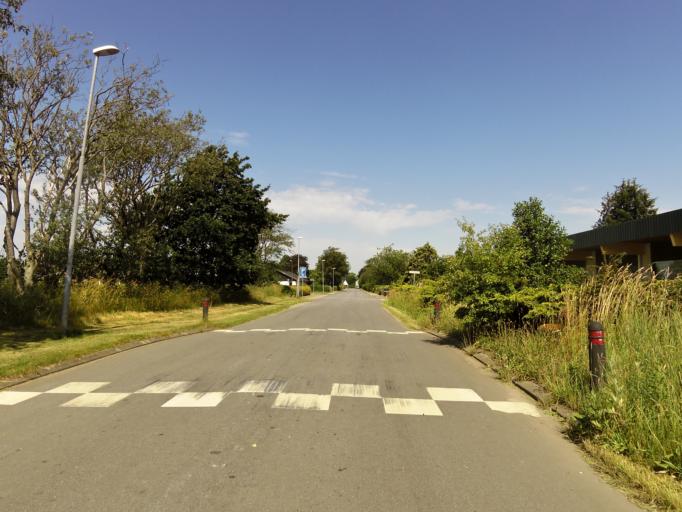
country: DK
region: South Denmark
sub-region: Haderslev Kommune
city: Vojens
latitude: 55.1971
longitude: 9.2150
